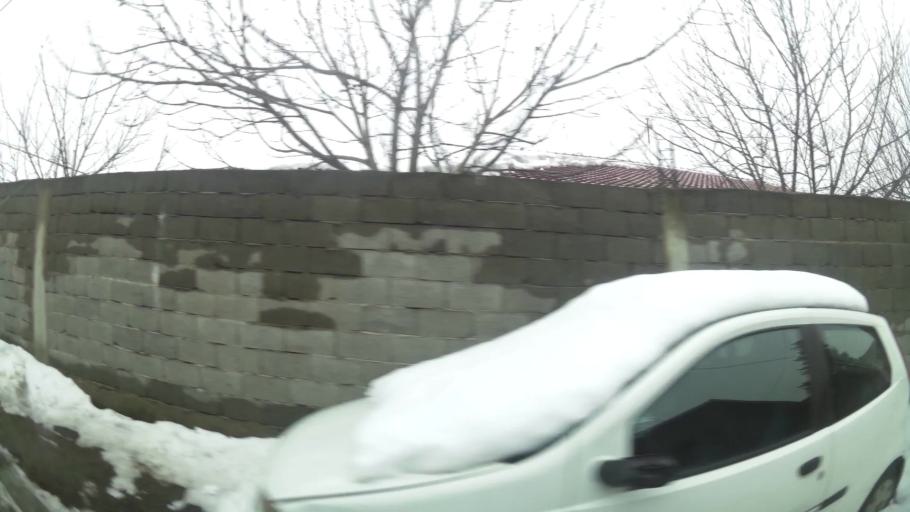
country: RS
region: Central Serbia
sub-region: Belgrade
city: Zvezdara
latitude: 44.7809
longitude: 20.5291
